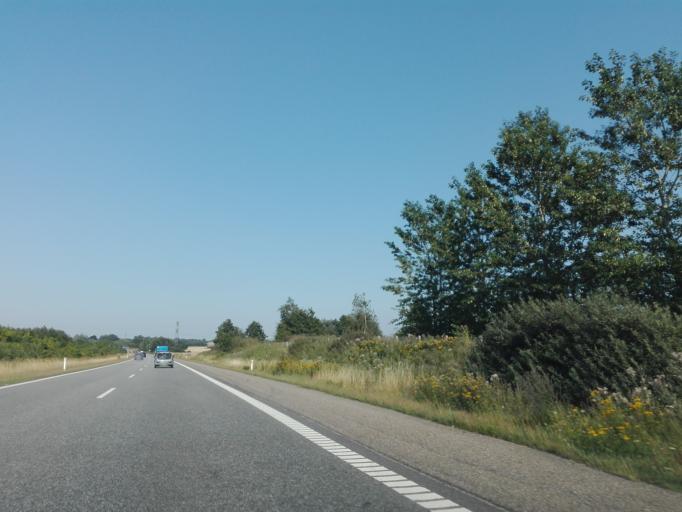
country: DK
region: Central Jutland
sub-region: Skanderborg Kommune
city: Horning
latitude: 56.1010
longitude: 10.0374
